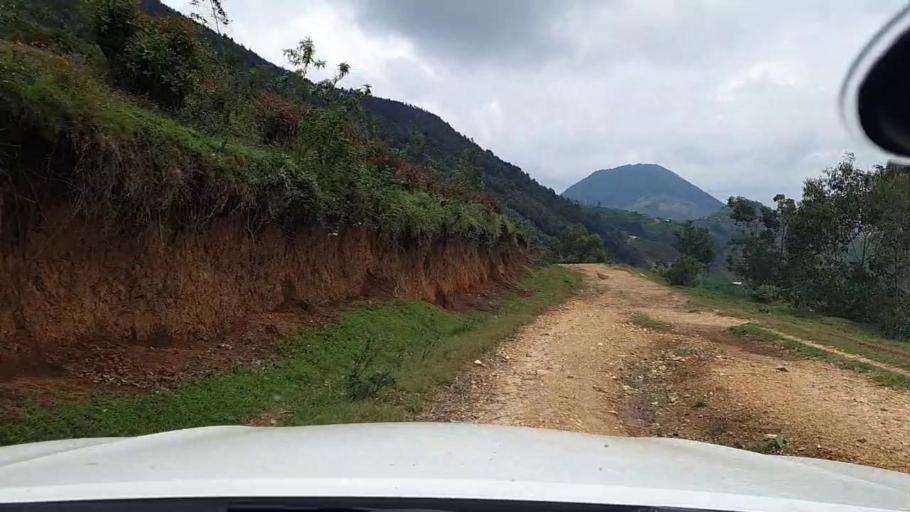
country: RW
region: Western Province
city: Kibuye
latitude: -2.1538
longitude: 29.4520
